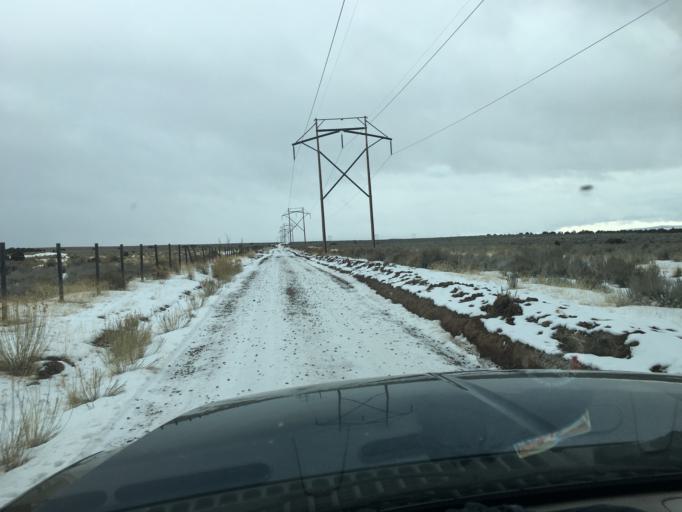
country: US
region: Colorado
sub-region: Garfield County
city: Parachute
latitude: 39.3437
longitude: -108.1698
